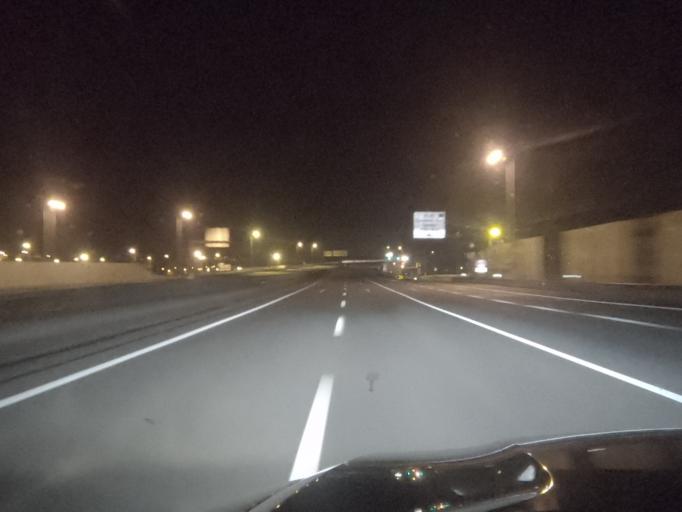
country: PT
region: Coimbra
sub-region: Coimbra
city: Coimbra
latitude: 40.1994
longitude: -8.4879
